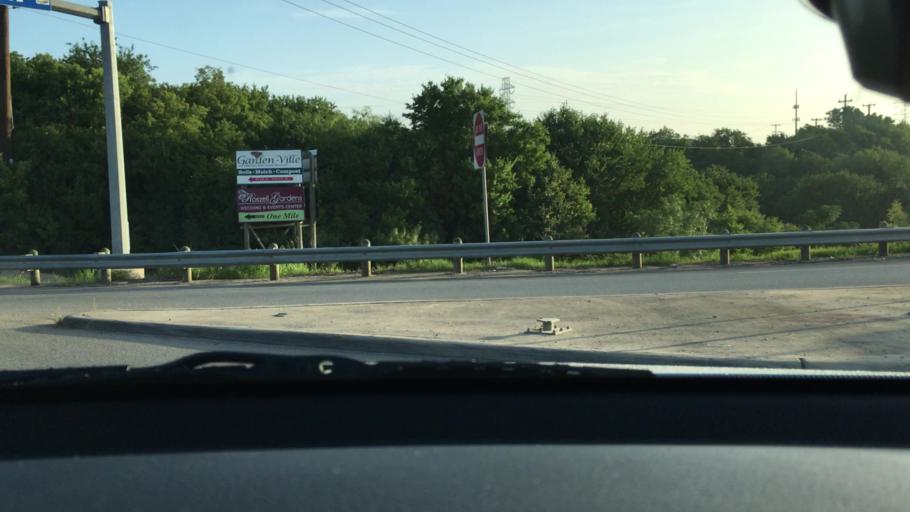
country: US
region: Texas
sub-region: Bexar County
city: Selma
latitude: 29.6044
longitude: -98.3277
